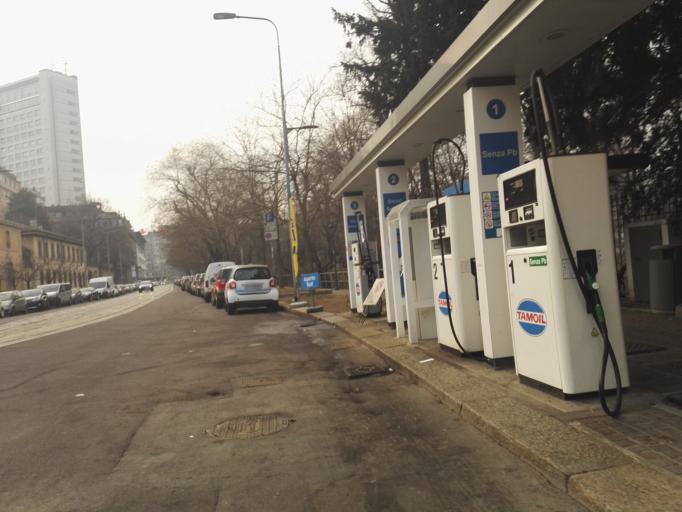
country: IT
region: Lombardy
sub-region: Citta metropolitana di Milano
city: Milano
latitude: 45.4731
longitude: 9.1995
